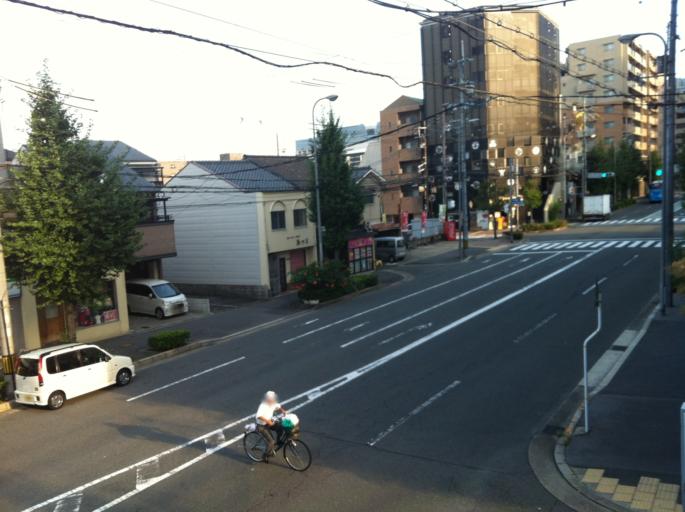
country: JP
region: Kyoto
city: Kyoto
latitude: 34.9815
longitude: 135.7599
